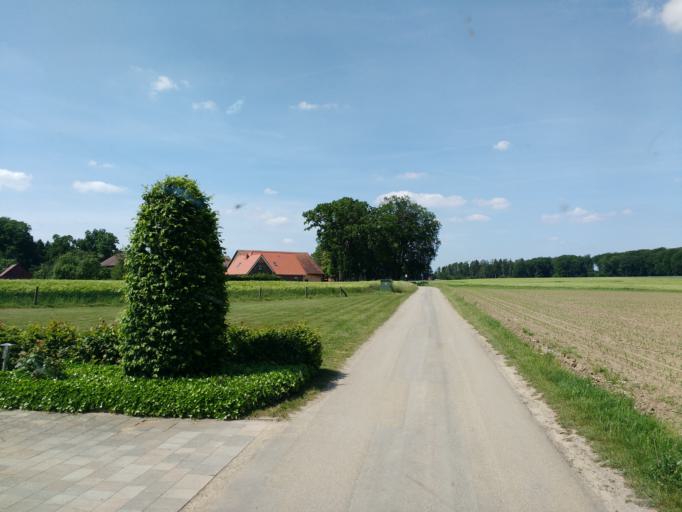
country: DE
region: Lower Saxony
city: Wallenhorst
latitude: 52.3713
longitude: 8.0871
